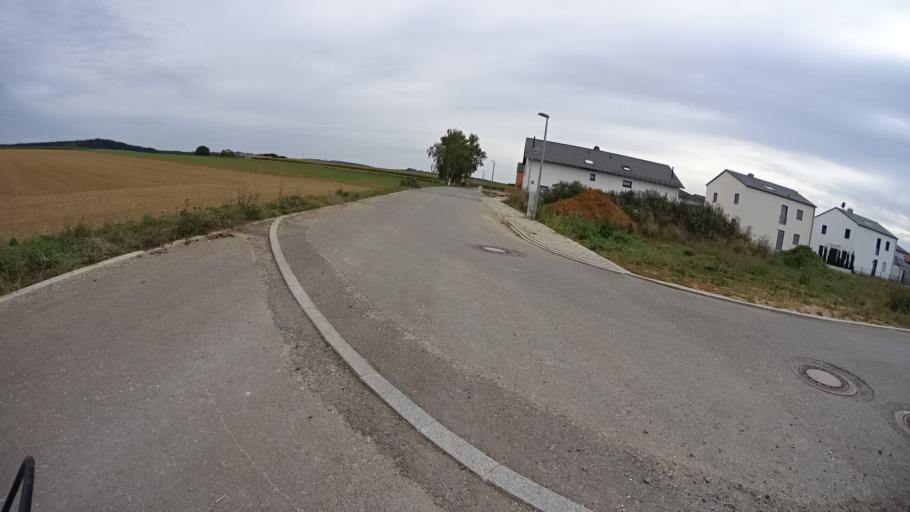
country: DE
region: Bavaria
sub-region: Upper Bavaria
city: Hitzhofen
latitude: 48.8771
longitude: 11.3320
